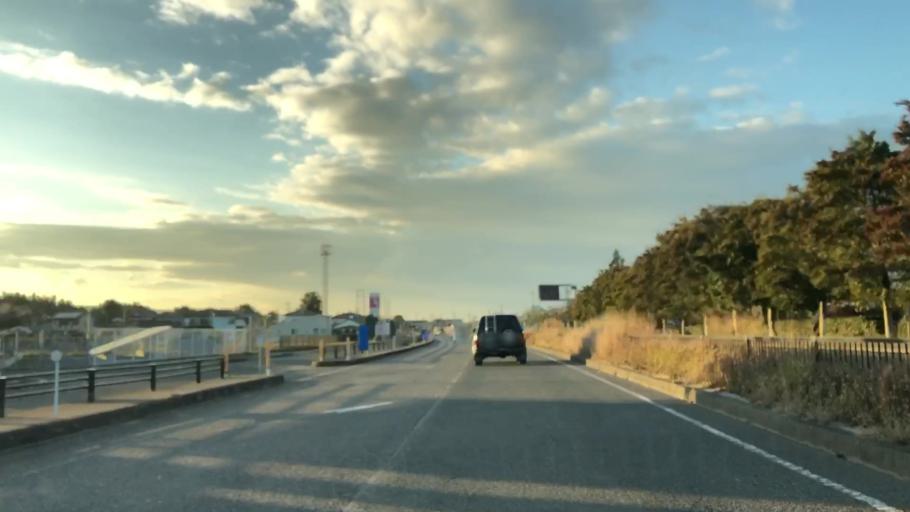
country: JP
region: Fukuoka
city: Nakatsu
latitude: 33.5592
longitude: 131.1988
